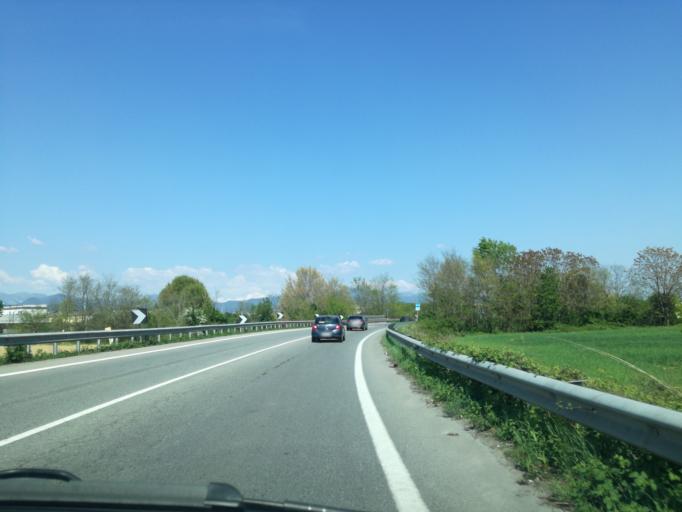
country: IT
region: Lombardy
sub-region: Provincia di Bergamo
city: Bonate Sopra
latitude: 45.6912
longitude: 9.5509
